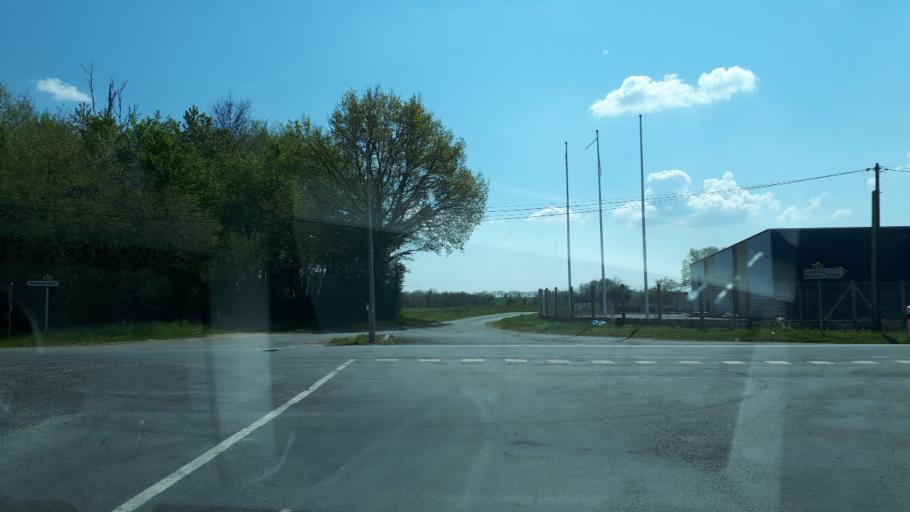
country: FR
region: Centre
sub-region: Departement du Cher
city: Henrichemont
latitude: 47.2981
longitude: 2.5121
